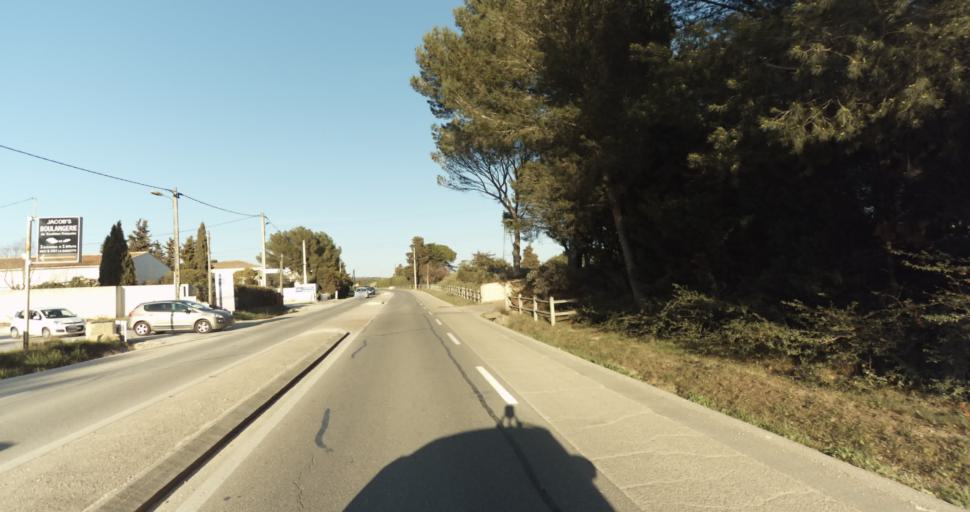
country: FR
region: Provence-Alpes-Cote d'Azur
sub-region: Departement des Bouches-du-Rhone
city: Velaux
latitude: 43.5410
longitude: 5.2709
